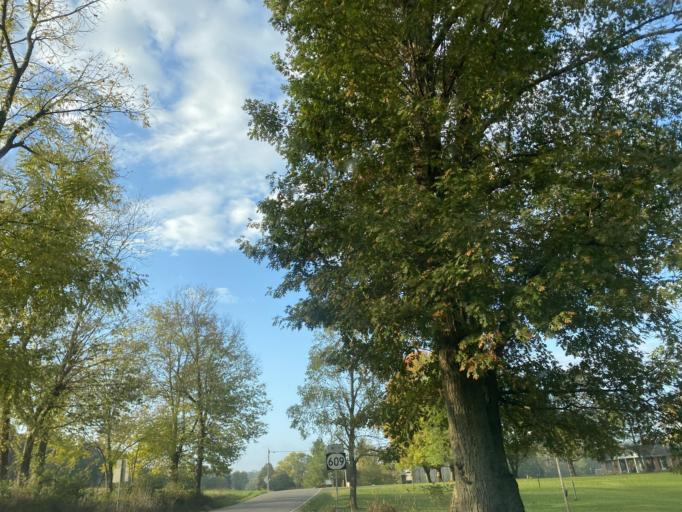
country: US
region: Kentucky
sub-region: Pendleton County
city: Falmouth
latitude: 38.7802
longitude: -84.3325
